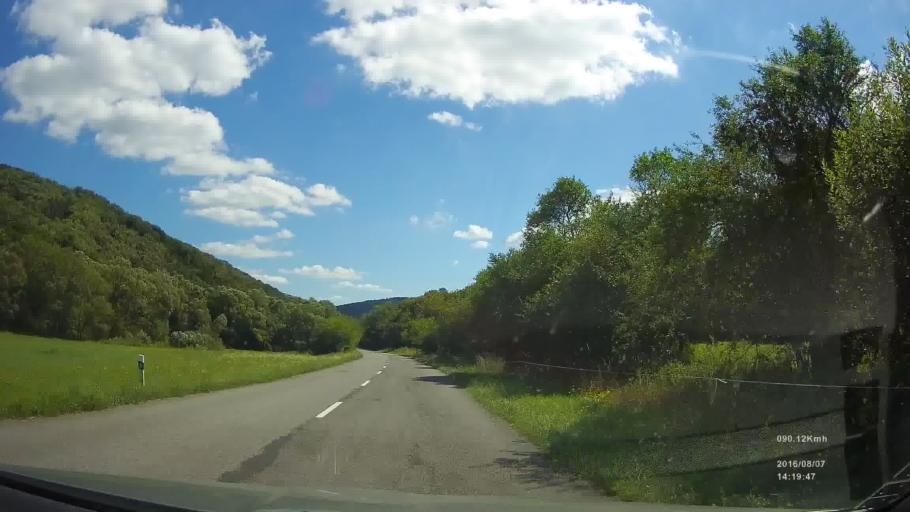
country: SK
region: Presovsky
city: Stropkov
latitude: 49.2985
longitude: 21.7561
